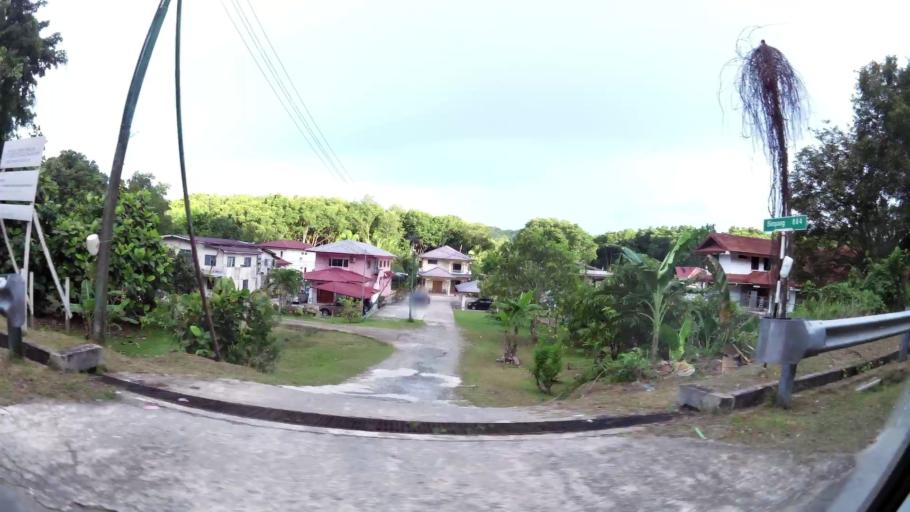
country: BN
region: Brunei and Muara
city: Bandar Seri Begawan
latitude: 4.9064
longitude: 114.9951
